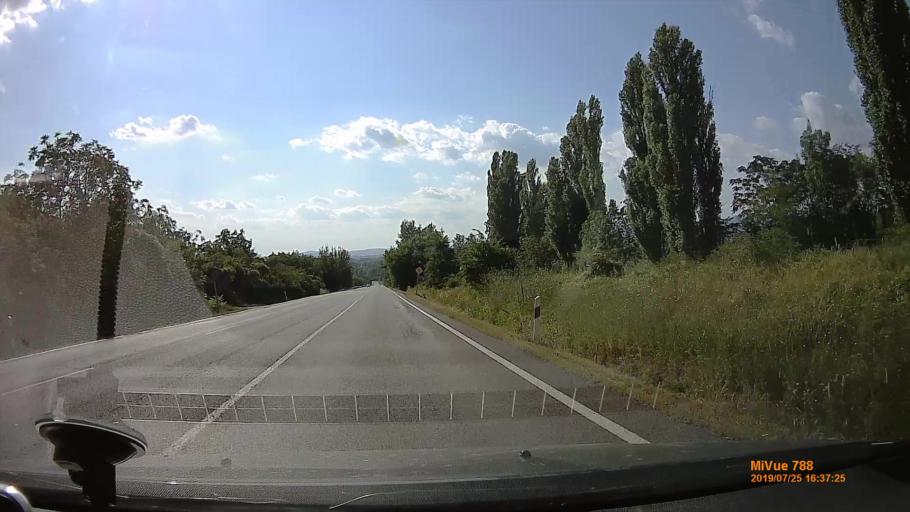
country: HU
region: Heves
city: Gyongyos
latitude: 47.7722
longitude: 19.9613
